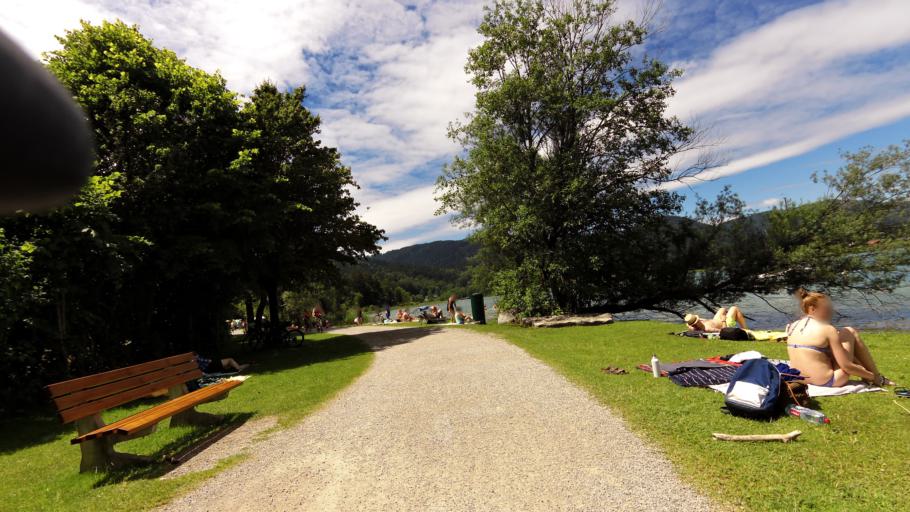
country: DE
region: Bavaria
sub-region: Upper Bavaria
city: Tegernsee
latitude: 47.6962
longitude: 11.7443
